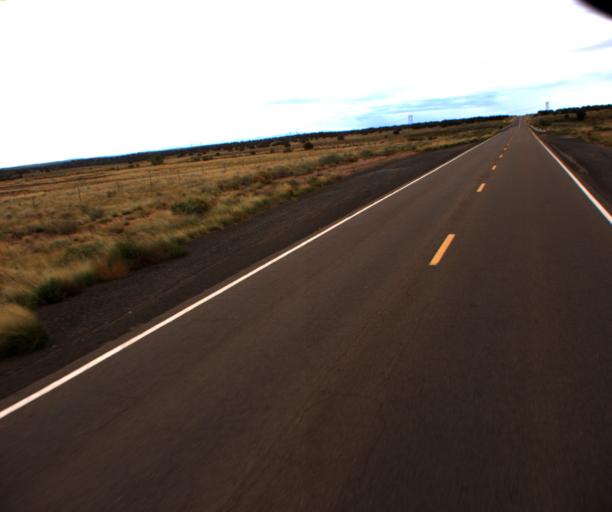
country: US
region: Arizona
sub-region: Navajo County
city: Snowflake
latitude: 34.6538
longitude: -110.0987
